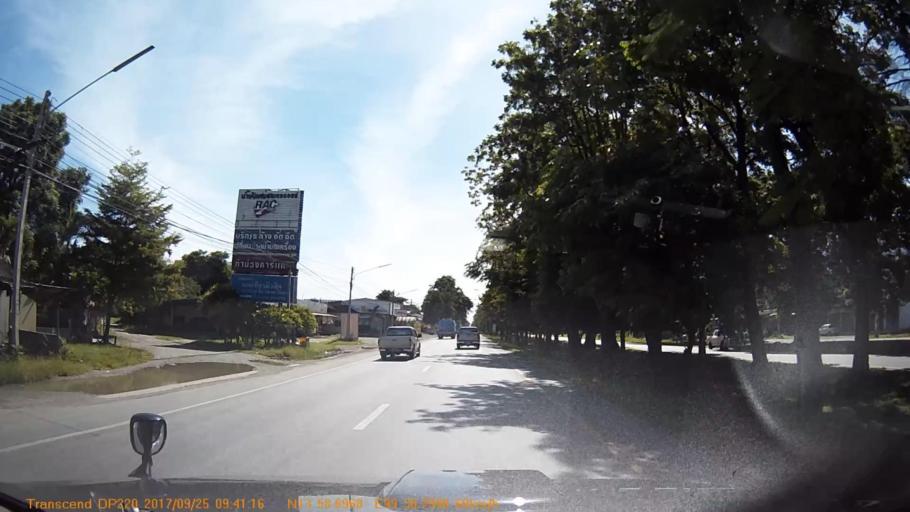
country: TH
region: Kanchanaburi
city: Tha Muang
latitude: 13.9783
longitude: 99.6467
